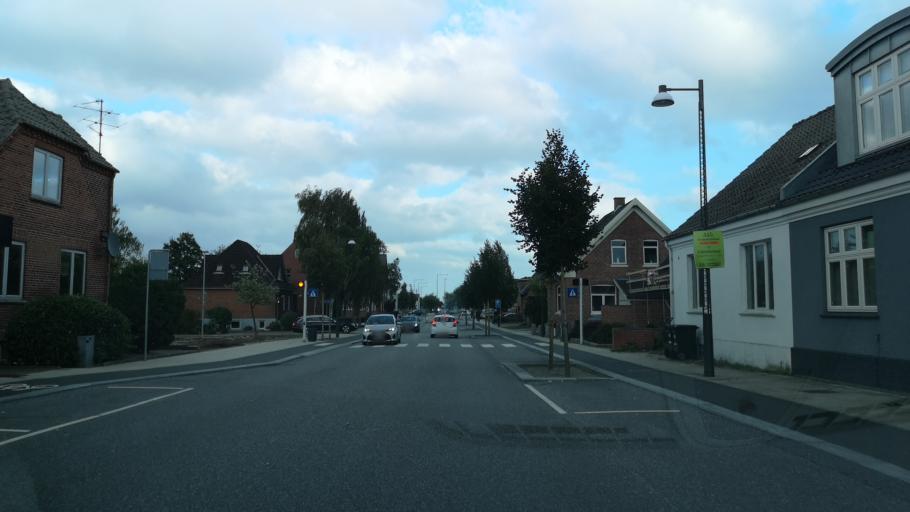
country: DK
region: Central Jutland
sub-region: Herning Kommune
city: Herning
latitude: 56.1348
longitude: 8.9900
